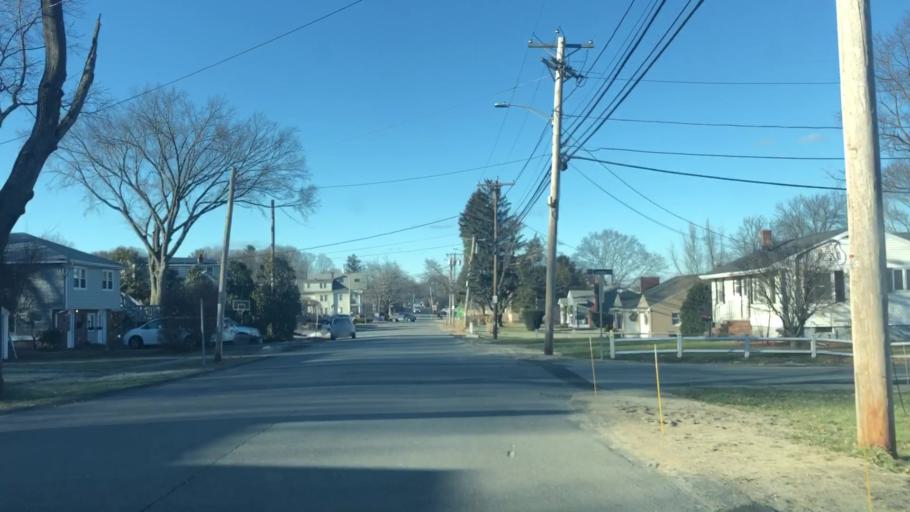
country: US
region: Massachusetts
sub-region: Essex County
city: North Andover
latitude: 42.6943
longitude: -71.1180
